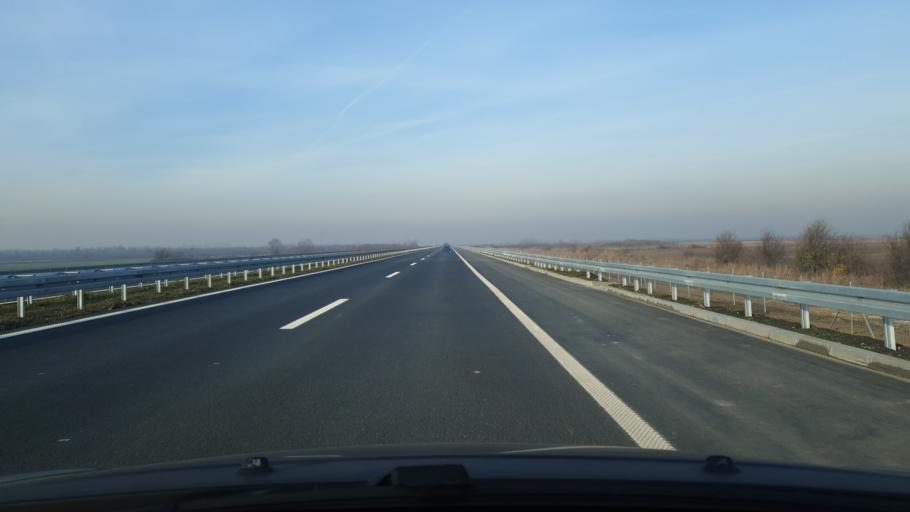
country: RS
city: Umka
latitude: 44.6960
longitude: 20.2658
